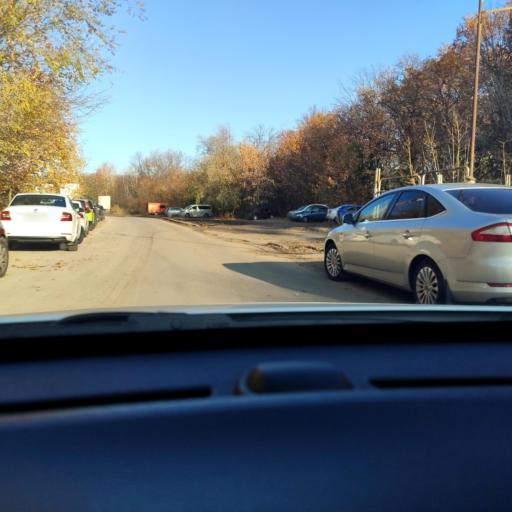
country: RU
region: Voronezj
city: Voronezh
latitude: 51.7275
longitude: 39.2123
